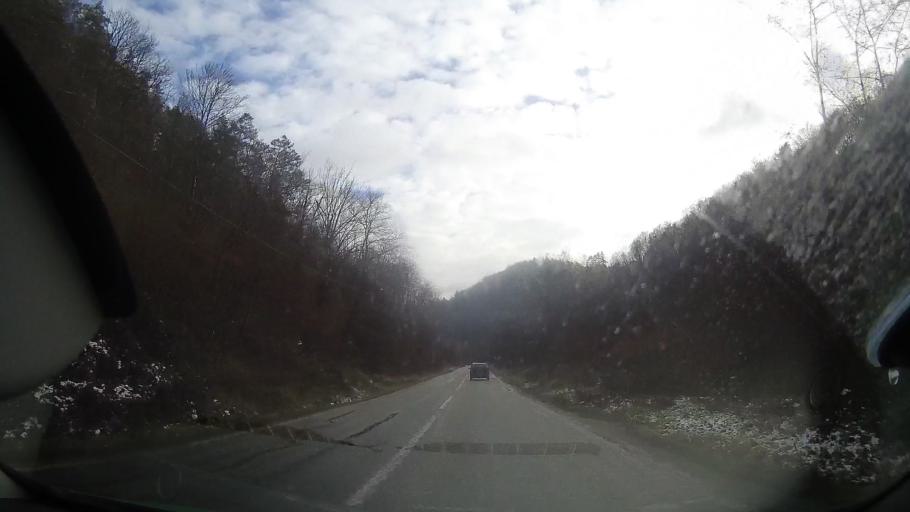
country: RO
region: Alba
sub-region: Oras Baia de Aries
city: Baia de Aries
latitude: 46.3820
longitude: 23.2631
